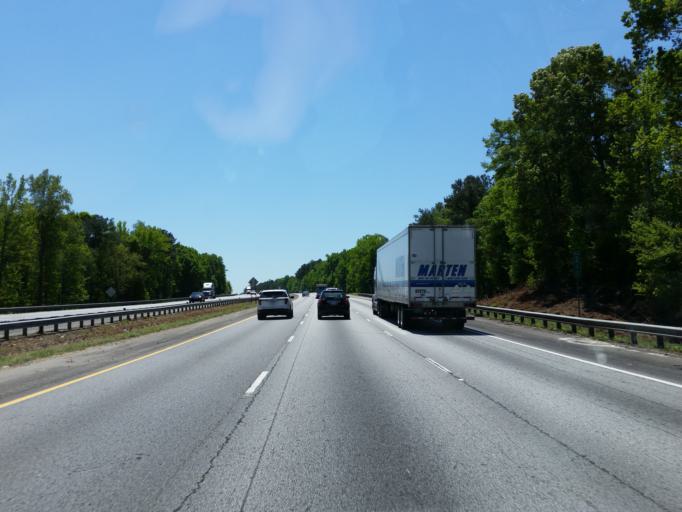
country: US
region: Georgia
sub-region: Henry County
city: Locust Grove
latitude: 33.3273
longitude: -84.1218
